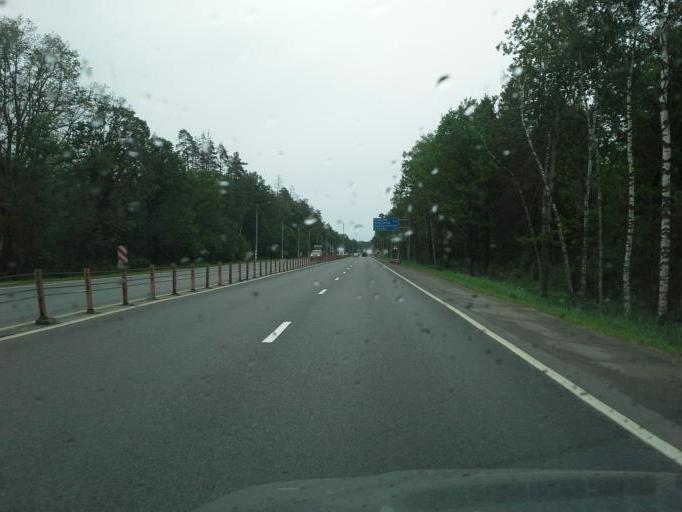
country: RU
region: Moskovskaya
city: Malaya Dubna
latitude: 55.8957
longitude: 39.0422
